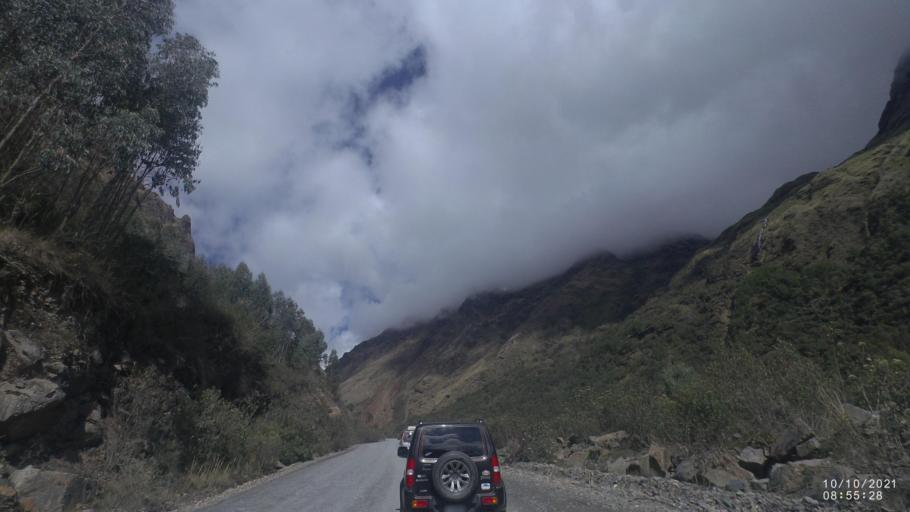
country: BO
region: La Paz
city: Quime
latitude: -16.9879
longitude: -67.2385
